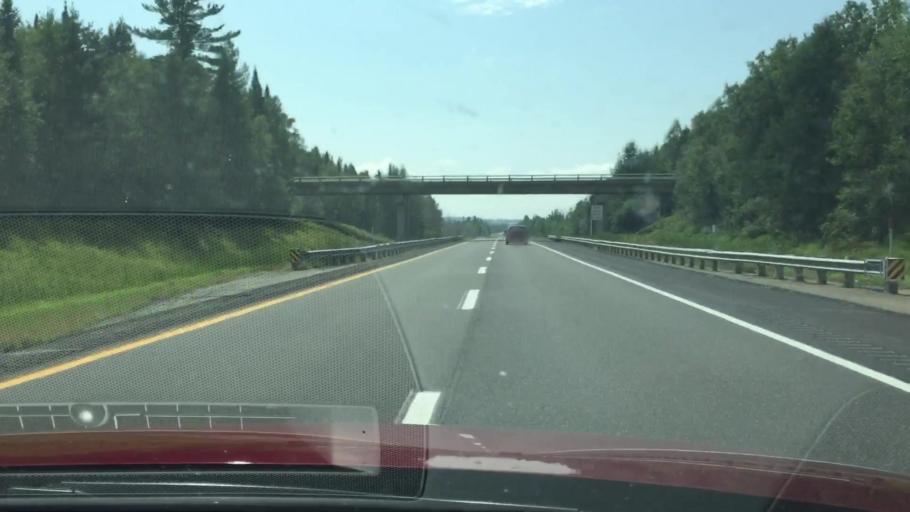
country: US
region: Maine
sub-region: Penobscot County
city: Patten
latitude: 45.9895
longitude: -68.2822
